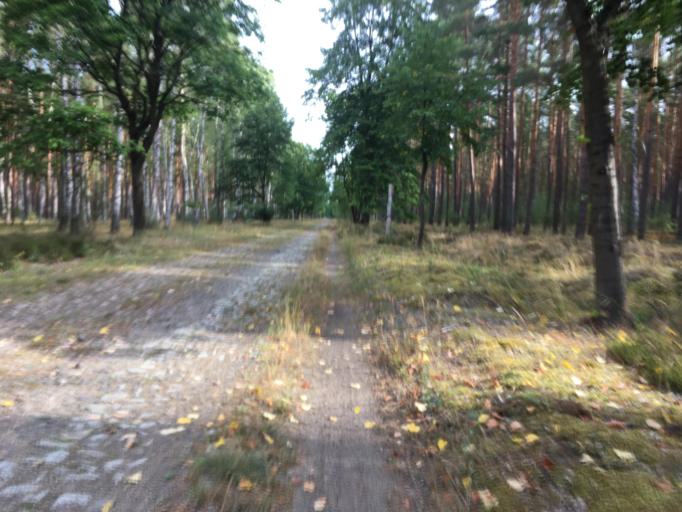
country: DE
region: Brandenburg
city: Marienwerder
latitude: 52.9402
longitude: 13.5215
